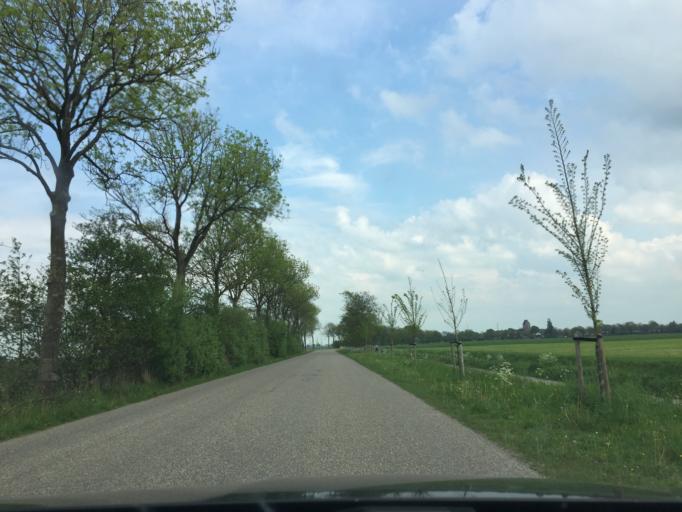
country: NL
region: Groningen
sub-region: Gemeente Zuidhorn
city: Oldehove
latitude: 53.3073
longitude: 6.3796
